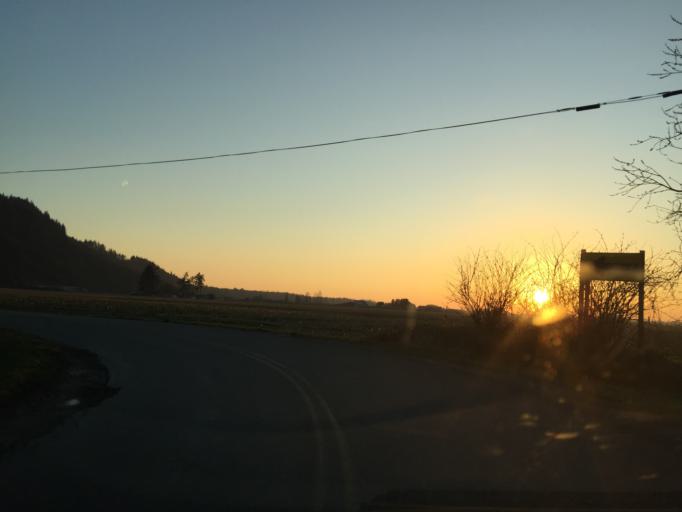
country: US
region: Washington
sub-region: Whatcom County
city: Sumas
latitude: 48.9863
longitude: -122.2038
